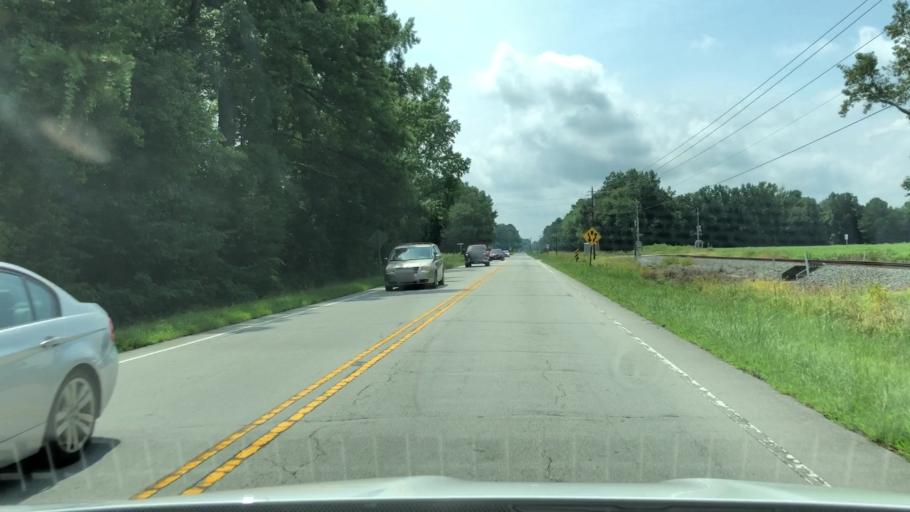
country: US
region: North Carolina
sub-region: Craven County
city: Vanceboro
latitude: 35.3399
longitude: -77.1511
